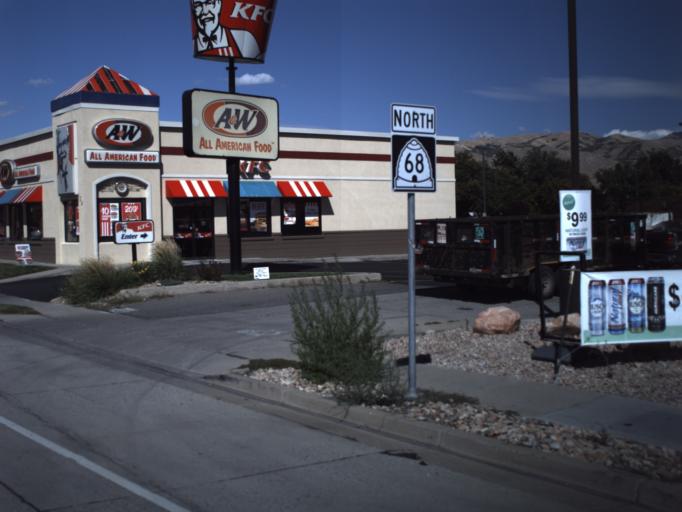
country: US
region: Utah
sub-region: Salt Lake County
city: Salt Lake City
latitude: 40.7719
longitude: -111.9392
